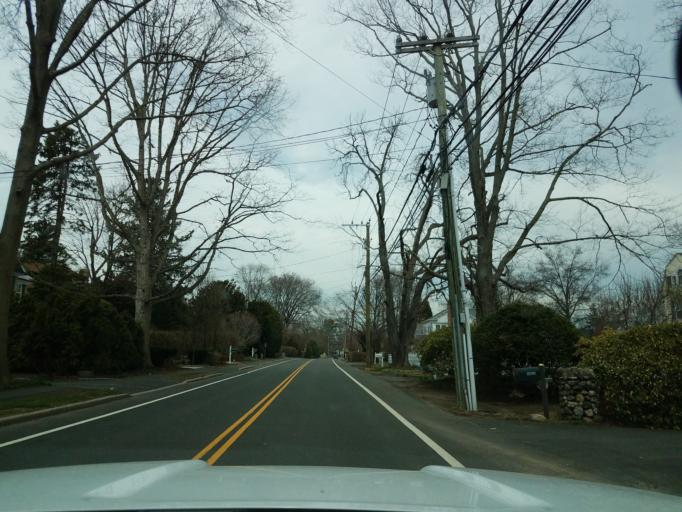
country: US
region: Connecticut
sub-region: Fairfield County
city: Old Greenwich
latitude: 41.0209
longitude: -73.5632
